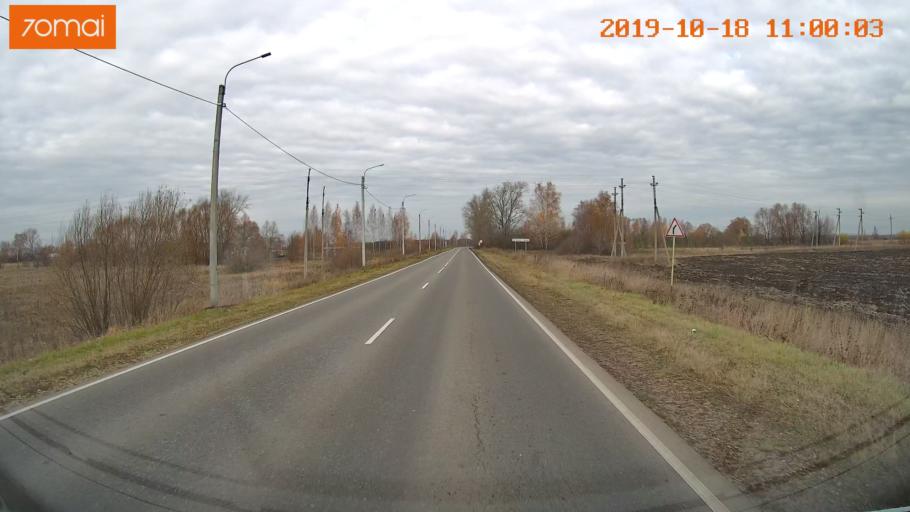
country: RU
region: Tula
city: Yepifan'
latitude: 53.8383
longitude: 38.5539
